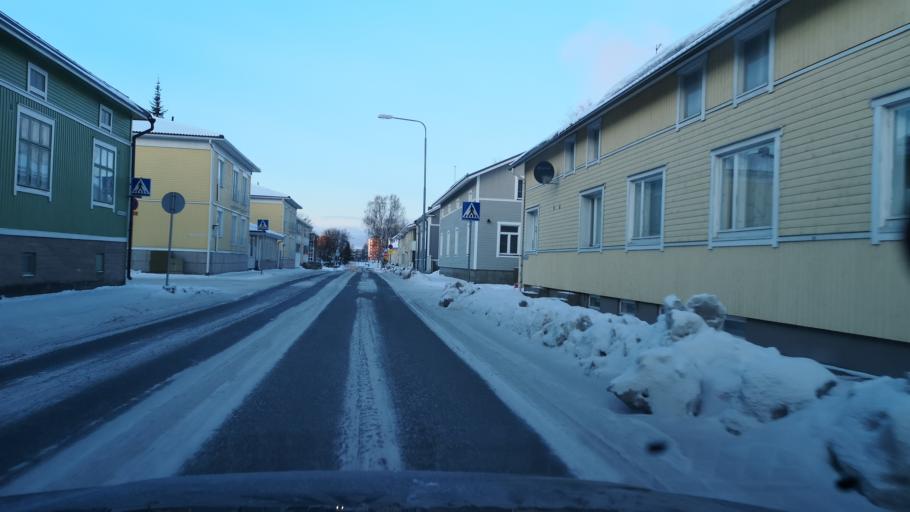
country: FI
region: Satakunta
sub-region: Pori
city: Pori
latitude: 61.4830
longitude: 21.8070
